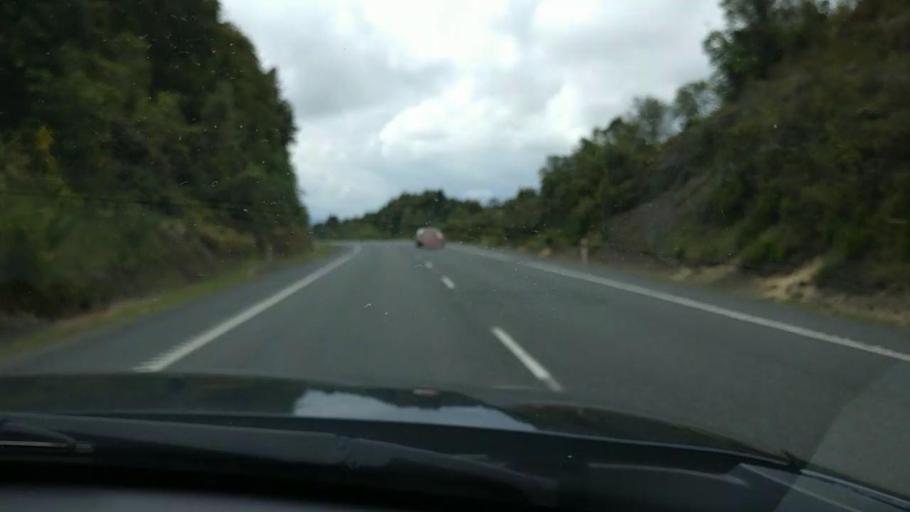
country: NZ
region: Bay of Plenty
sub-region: Rotorua District
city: Rotorua
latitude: -38.0719
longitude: 176.1280
